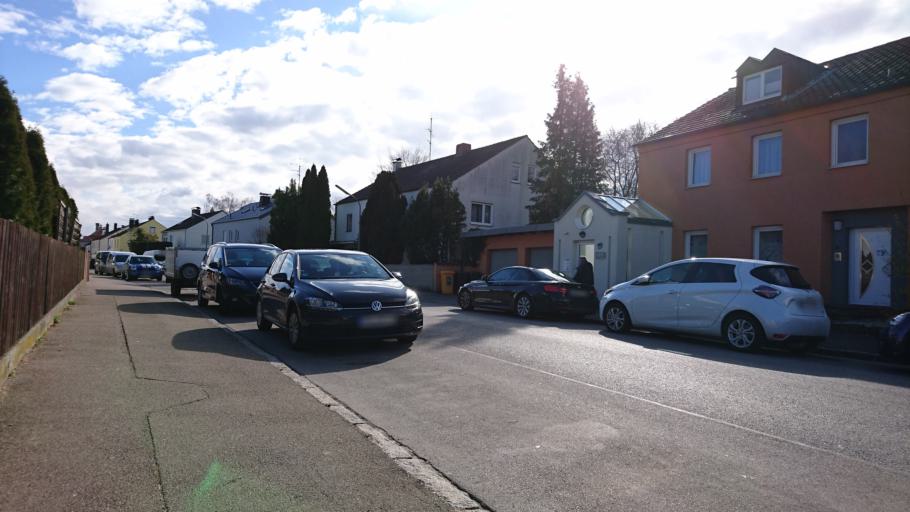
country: DE
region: Bavaria
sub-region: Swabia
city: Augsburg
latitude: 48.3831
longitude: 10.9129
